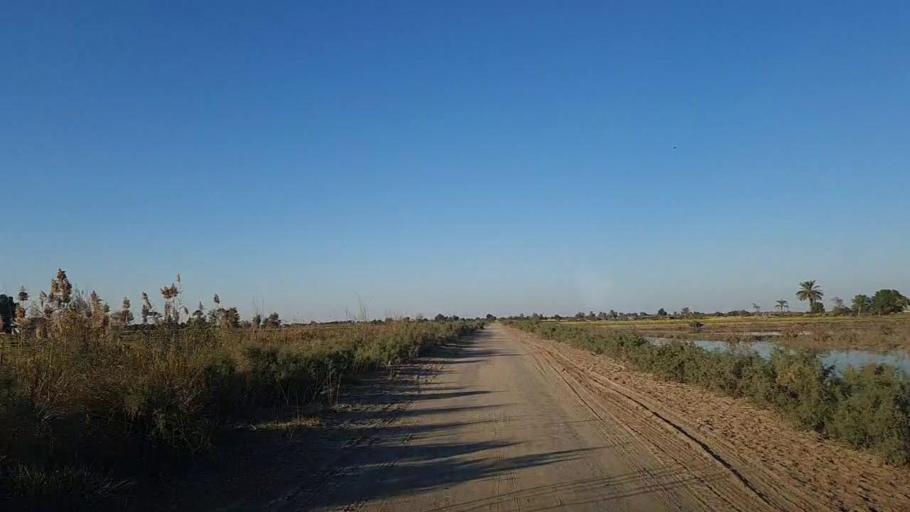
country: PK
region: Sindh
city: Sanghar
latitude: 26.1429
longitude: 68.9265
